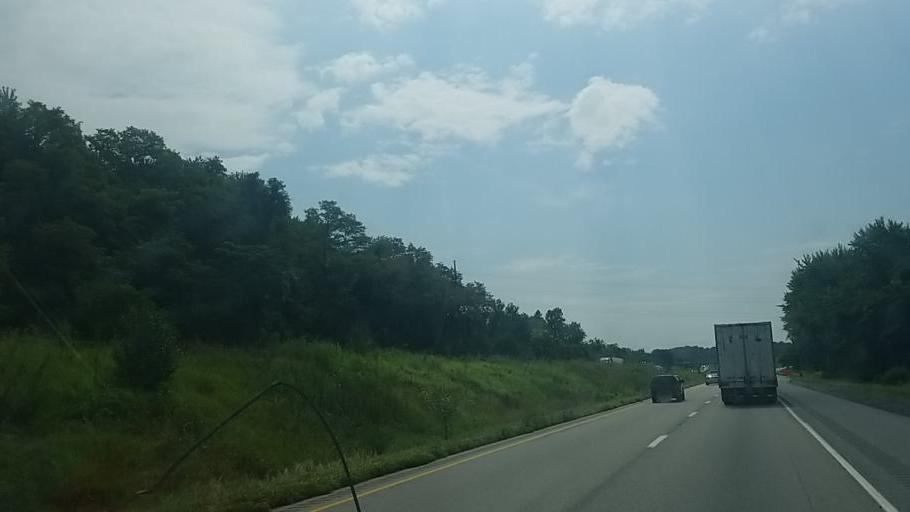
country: US
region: Pennsylvania
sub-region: Perry County
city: Marysville
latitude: 40.3306
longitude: -76.8968
